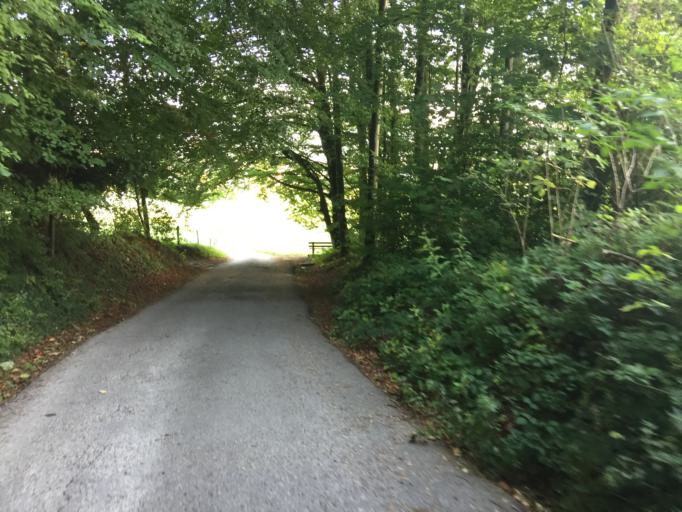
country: CH
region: Saint Gallen
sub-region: Wahlkreis Wil
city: Oberuzwil
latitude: 47.4152
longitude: 9.1427
